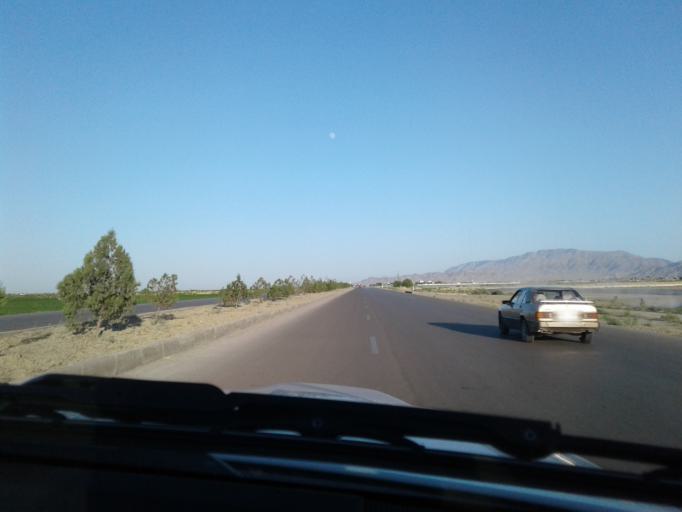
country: TM
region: Ahal
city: Baharly
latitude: 38.3329
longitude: 57.5763
